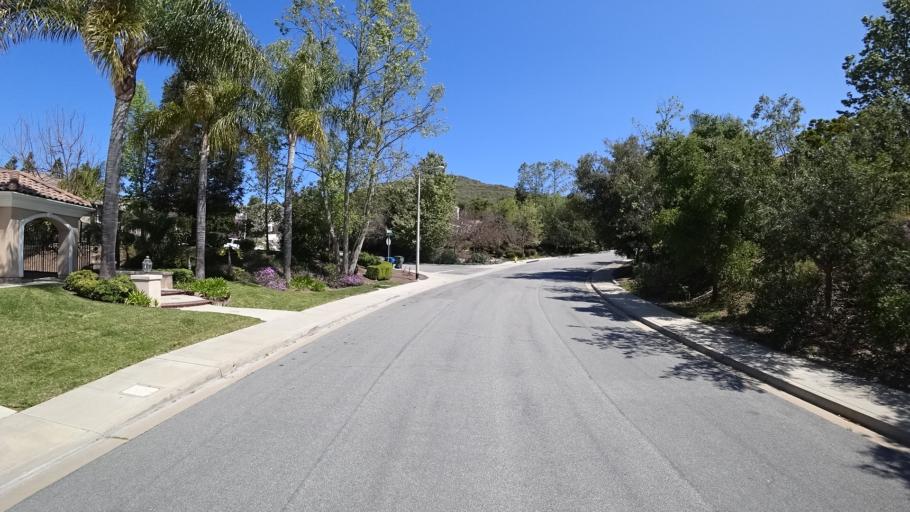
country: US
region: California
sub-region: Ventura County
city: Moorpark
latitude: 34.2314
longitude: -118.8850
